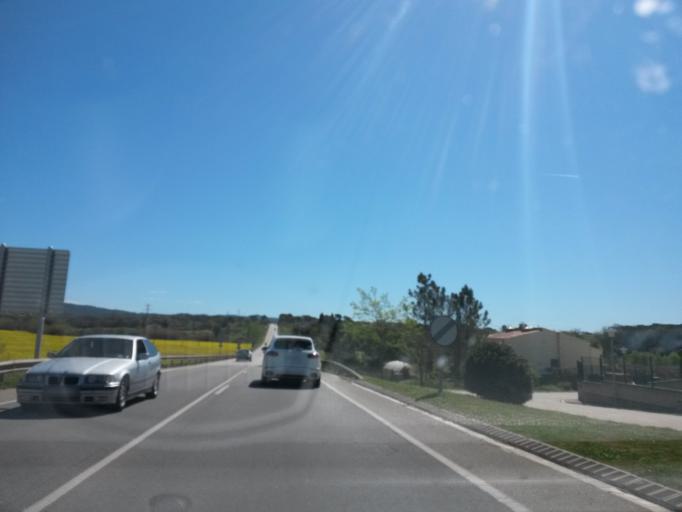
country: ES
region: Catalonia
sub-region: Provincia de Girona
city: Riudellots de la Selva
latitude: 41.8964
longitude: 2.8332
